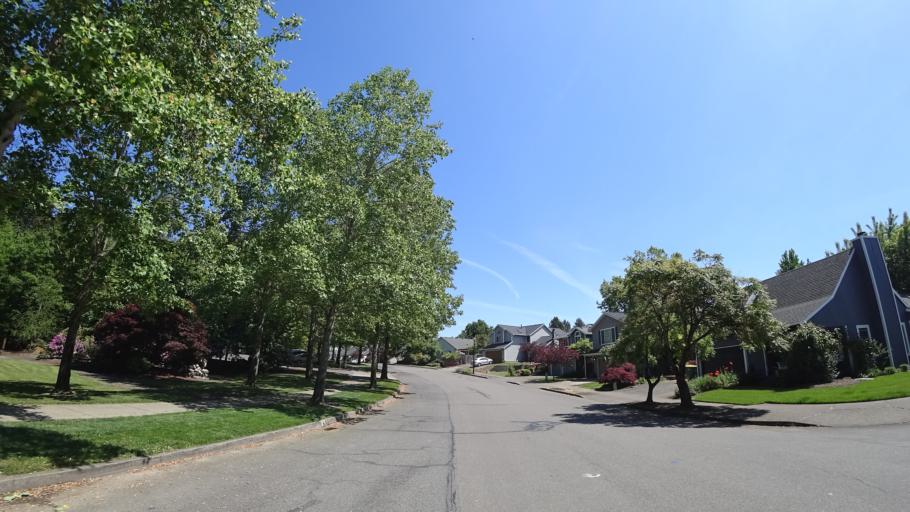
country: US
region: Oregon
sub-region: Washington County
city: King City
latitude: 45.4365
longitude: -122.8113
